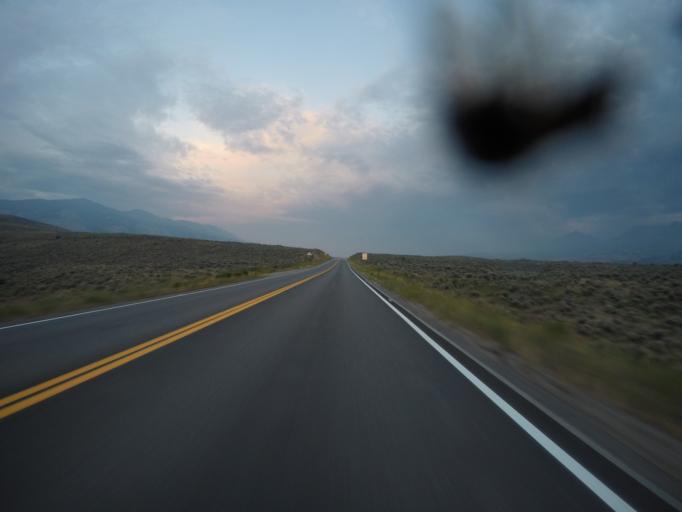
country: US
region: Colorado
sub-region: Grand County
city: Kremmling
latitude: 39.8828
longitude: -106.2824
